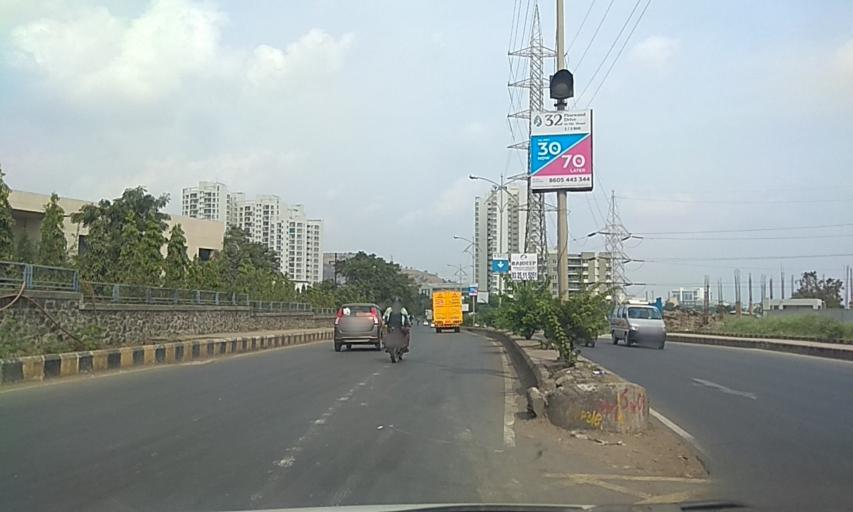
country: IN
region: Maharashtra
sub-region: Pune Division
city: Pimpri
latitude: 18.5891
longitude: 73.7052
